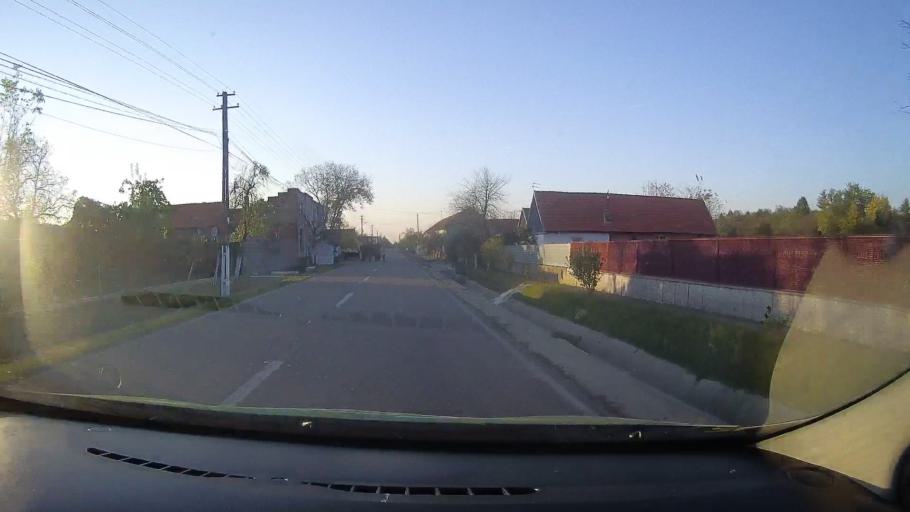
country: RO
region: Timis
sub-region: Comuna Traian Vuia
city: Traian Vuia
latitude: 45.7951
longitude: 22.0690
